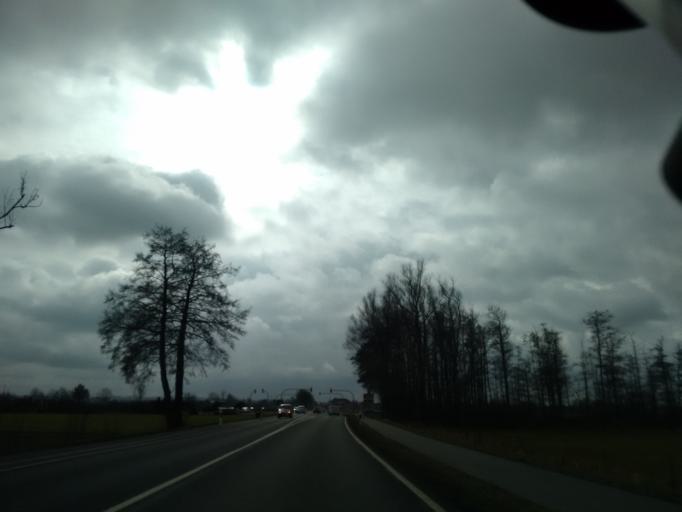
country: DE
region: North Rhine-Westphalia
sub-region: Regierungsbezirk Detmold
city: Paderborn
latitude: 51.7516
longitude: 8.7779
